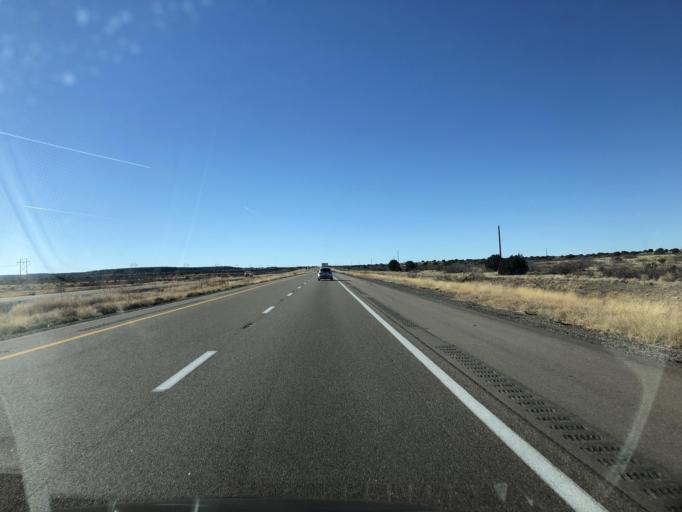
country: US
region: New Mexico
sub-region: Quay County
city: Tucumcari
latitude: 35.0771
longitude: -104.1401
